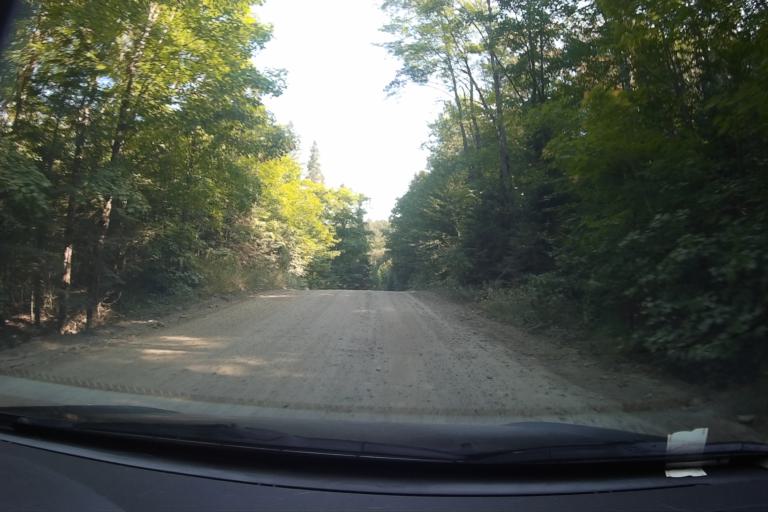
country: CA
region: Ontario
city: Huntsville
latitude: 45.5439
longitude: -78.6959
